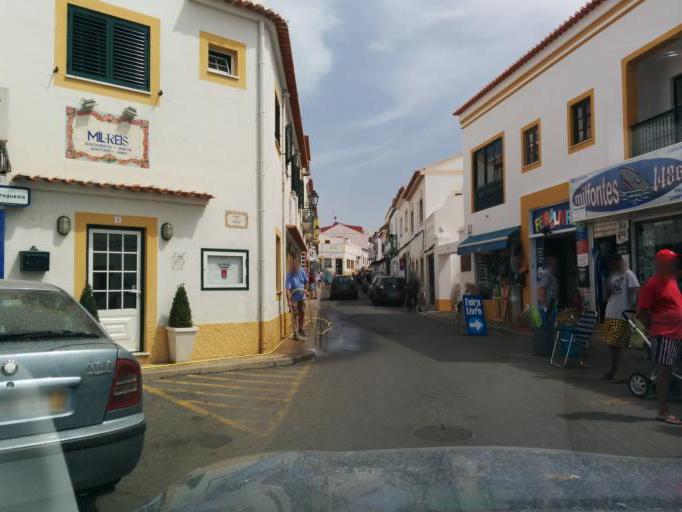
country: PT
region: Beja
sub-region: Odemira
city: Vila Nova de Milfontes
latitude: 37.7240
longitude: -8.7818
